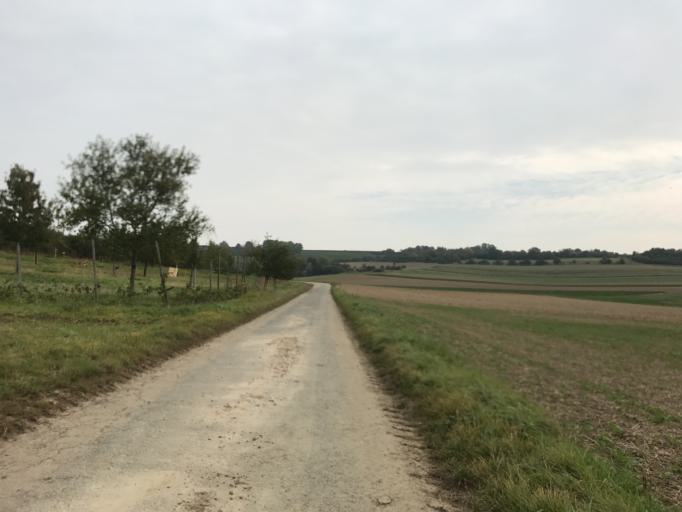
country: DE
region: Rheinland-Pfalz
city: Klein-Winternheim
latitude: 49.9278
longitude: 8.2199
